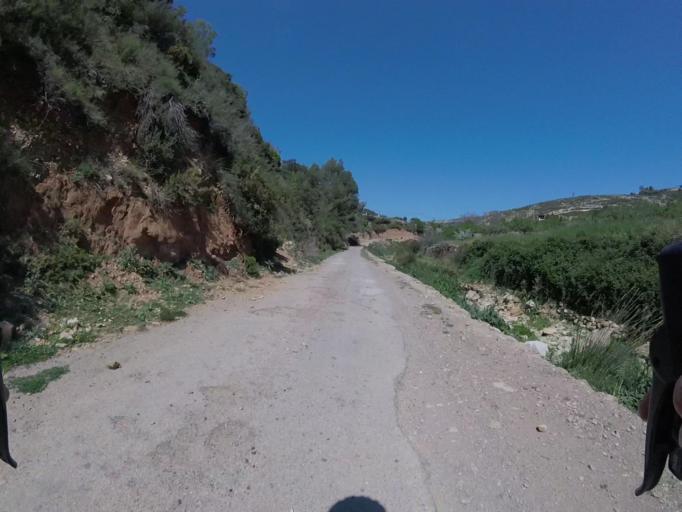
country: ES
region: Valencia
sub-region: Provincia de Castello
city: Sierra-Engarceran
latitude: 40.2608
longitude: -0.0232
